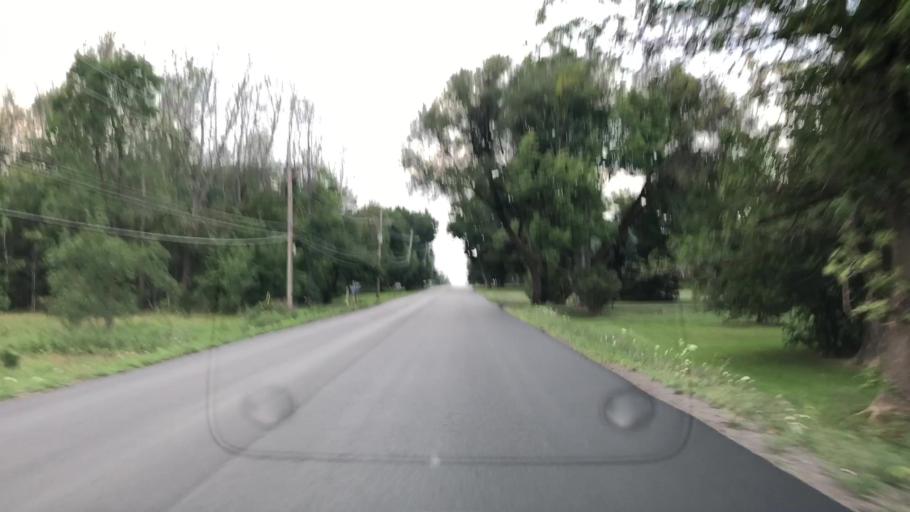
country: US
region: New York
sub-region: Erie County
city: Elma Center
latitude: 42.8133
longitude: -78.6059
